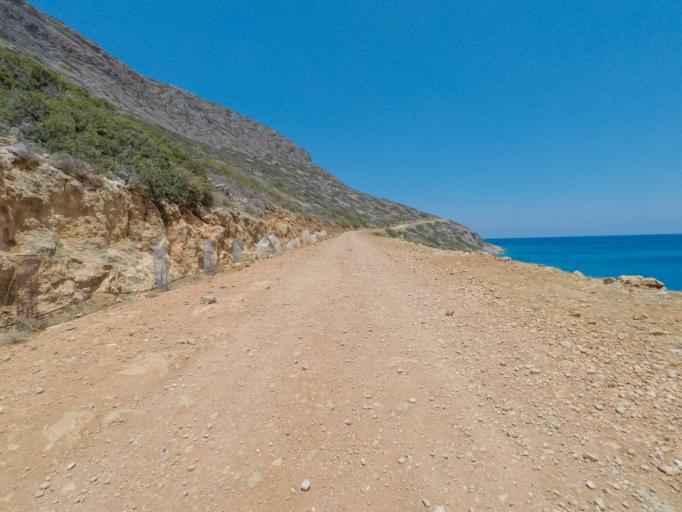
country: GR
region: Crete
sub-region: Nomos Lasithiou
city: Elounda
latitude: 35.3070
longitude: 25.7356
